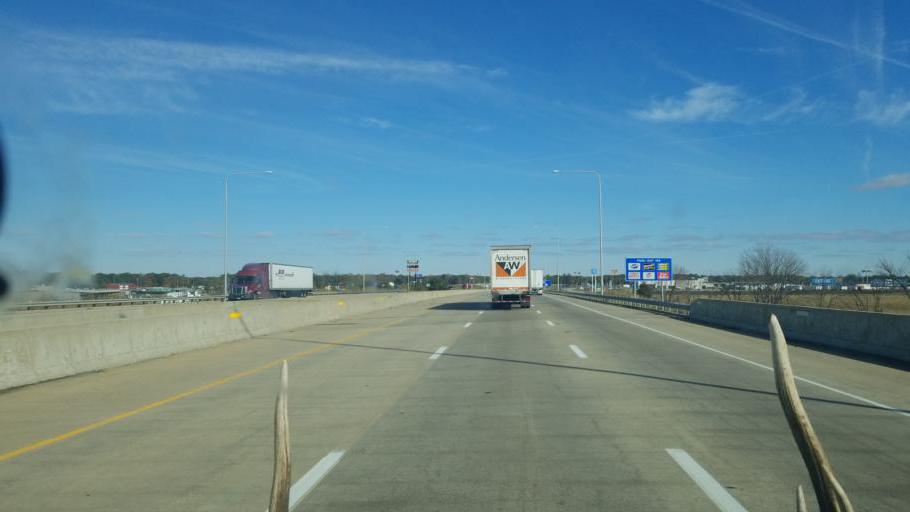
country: US
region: Illinois
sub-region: Effingham County
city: Effingham
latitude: 39.1115
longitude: -88.5713
